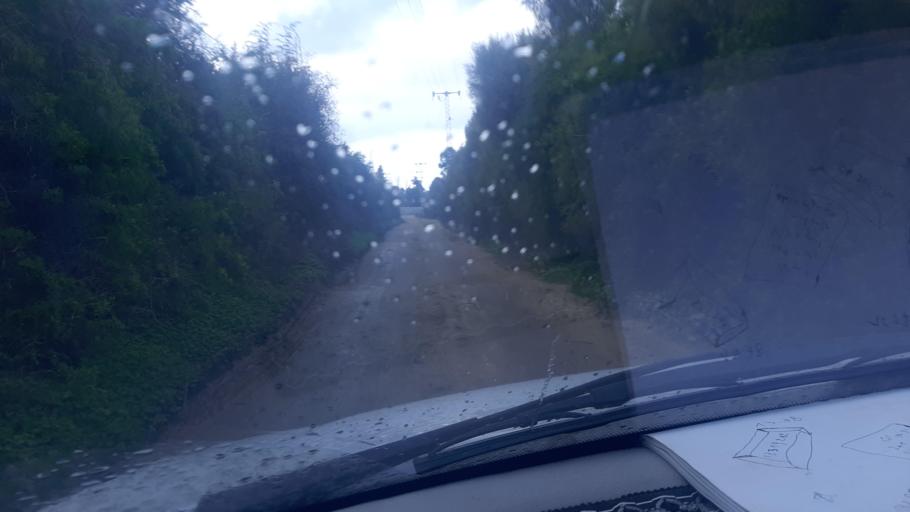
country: TN
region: Nabul
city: Manzil Bu Zalafah
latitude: 36.7412
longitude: 10.5287
